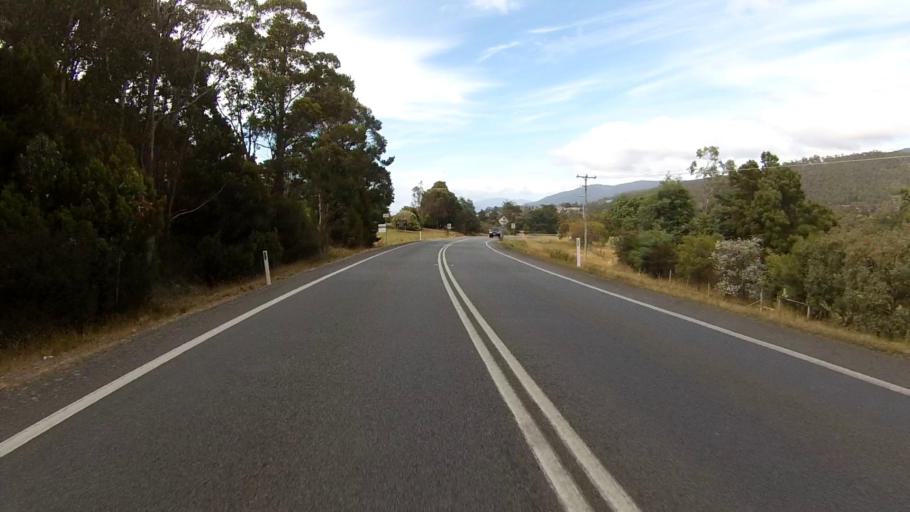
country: AU
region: Tasmania
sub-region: Kingborough
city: Kettering
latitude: -43.1142
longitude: 147.2449
